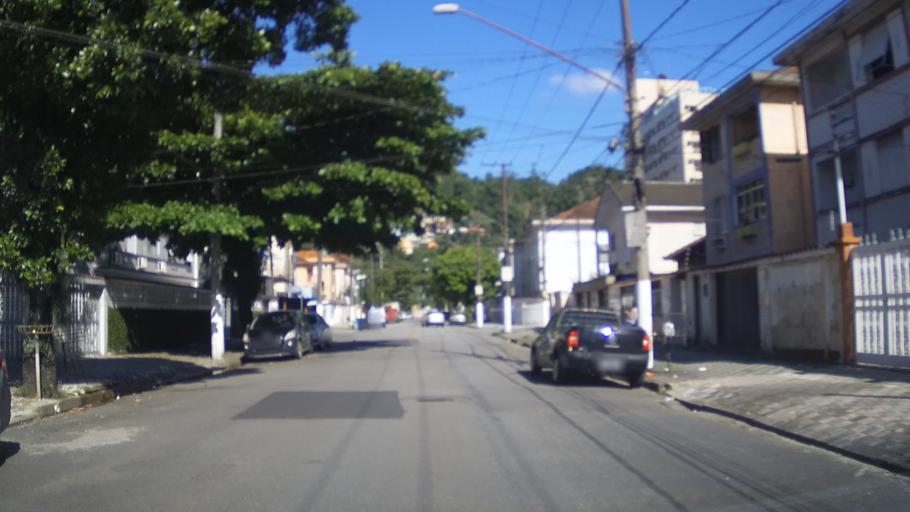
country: BR
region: Sao Paulo
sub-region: Santos
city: Santos
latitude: -23.9544
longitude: -46.3485
